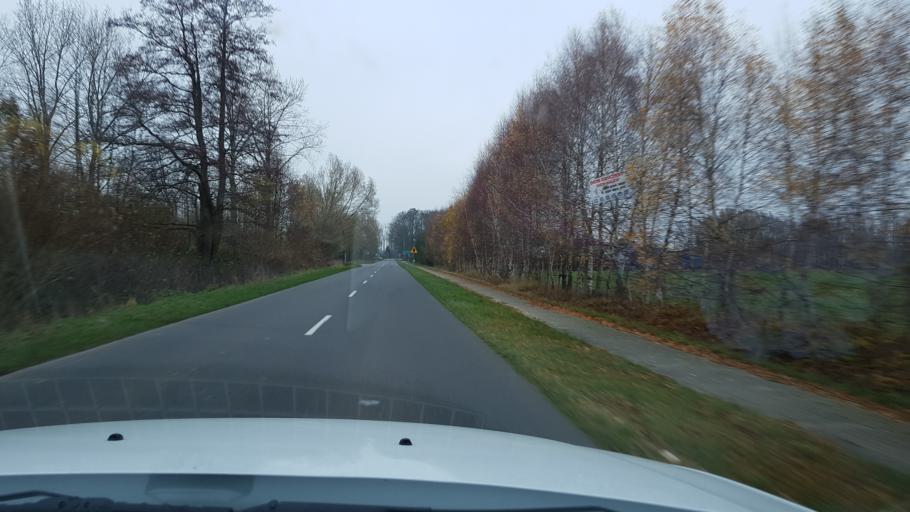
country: PL
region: West Pomeranian Voivodeship
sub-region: Powiat kamienski
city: Kamien Pomorski
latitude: 53.9477
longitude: 14.6794
